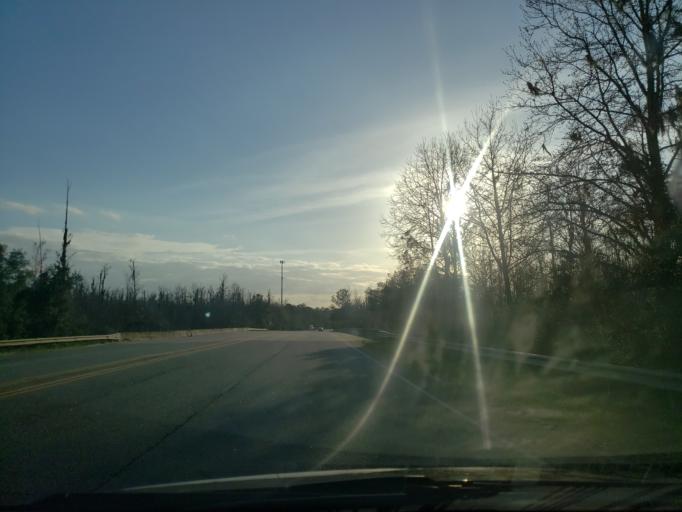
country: US
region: Georgia
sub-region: Chatham County
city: Bloomingdale
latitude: 32.1530
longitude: -81.2788
